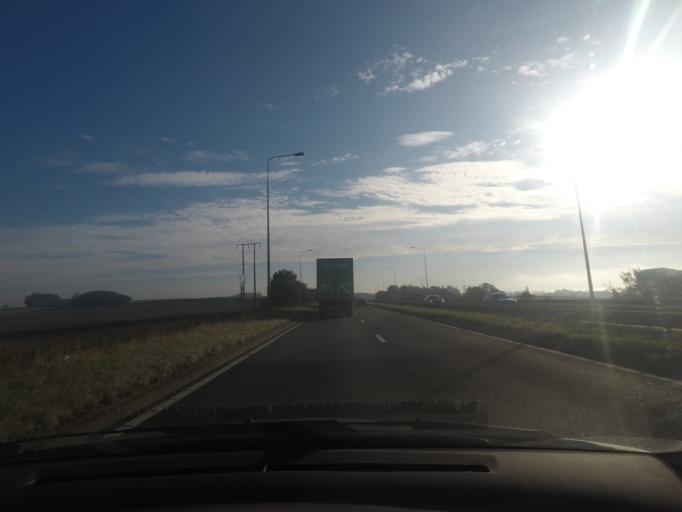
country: GB
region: England
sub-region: East Riding of Yorkshire
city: North Ferriby
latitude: 53.7258
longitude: -0.4903
